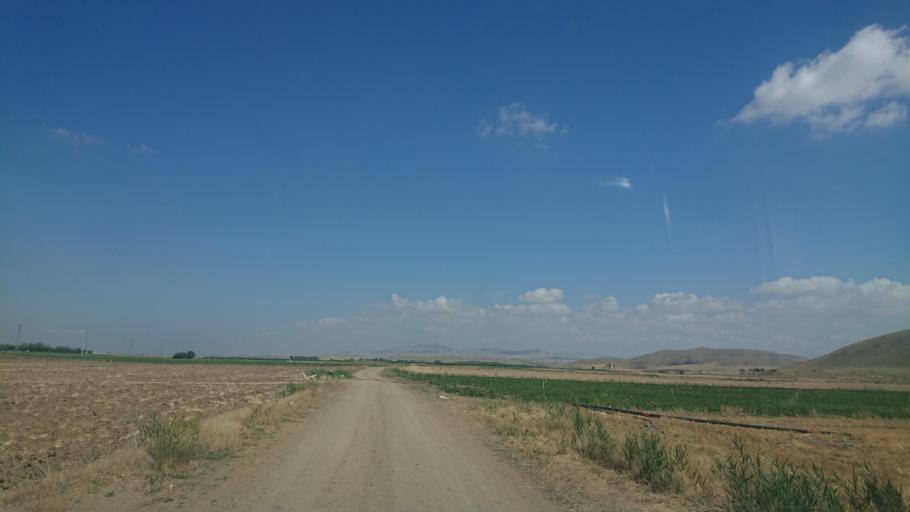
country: TR
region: Aksaray
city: Sariyahsi
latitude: 38.9792
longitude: 33.9103
